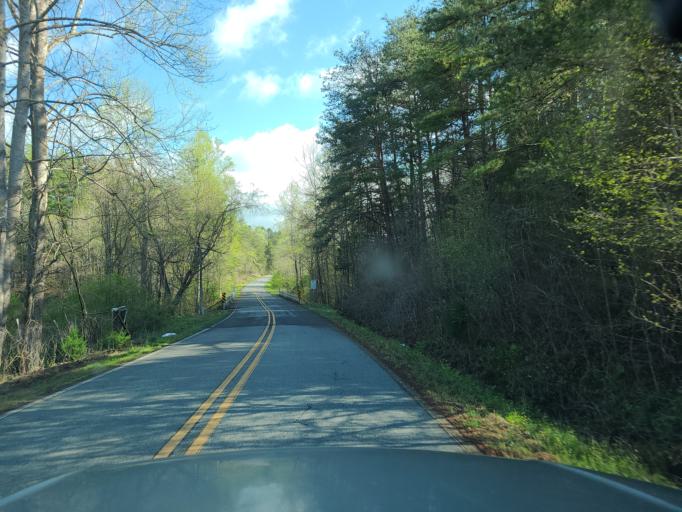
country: US
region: North Carolina
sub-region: Rutherford County
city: Forest City
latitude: 35.4093
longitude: -81.8205
